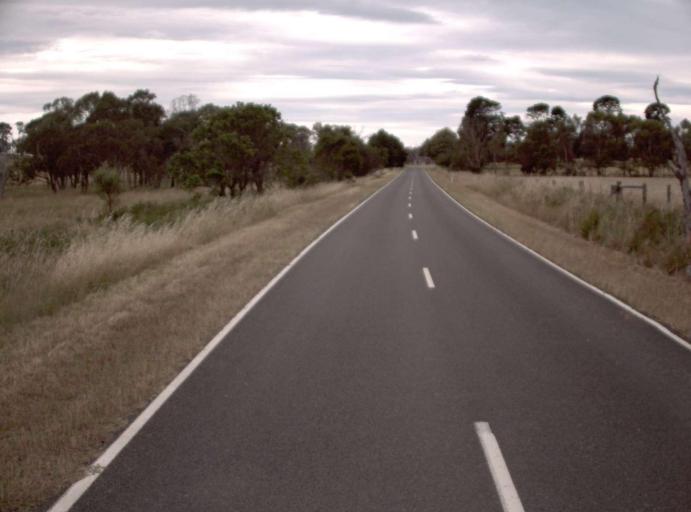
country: AU
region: Victoria
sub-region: East Gippsland
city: Bairnsdale
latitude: -37.9752
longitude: 147.4401
